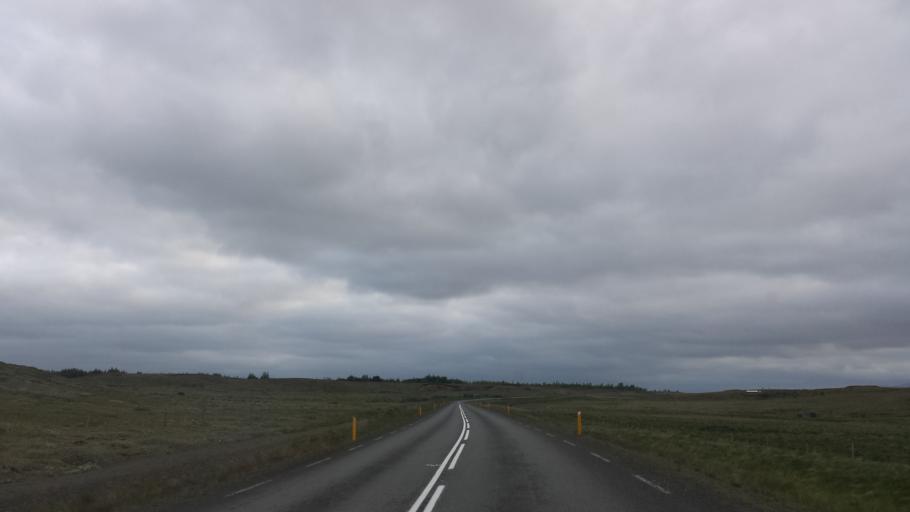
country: IS
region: South
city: Selfoss
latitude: 64.1232
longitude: -20.6013
